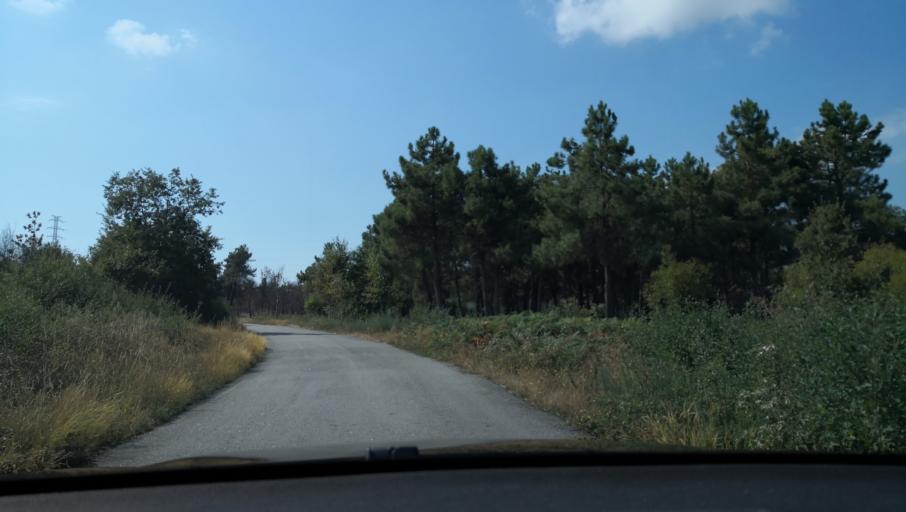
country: PT
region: Vila Real
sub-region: Sabrosa
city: Sabrosa
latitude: 41.3303
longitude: -7.6146
